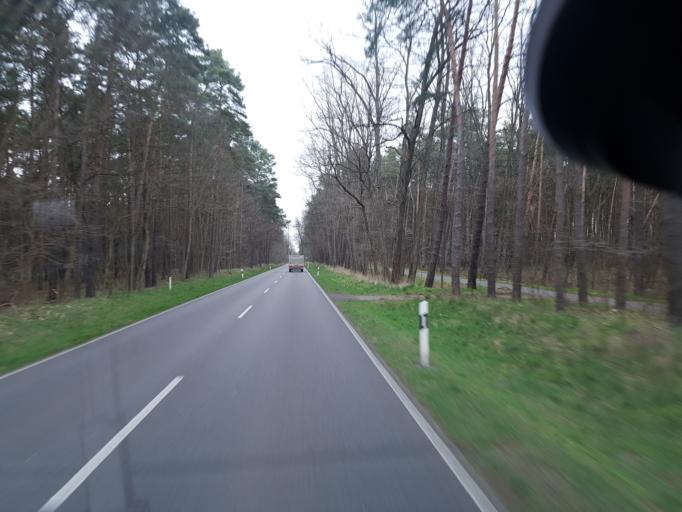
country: DE
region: Brandenburg
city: Tauche
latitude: 52.1281
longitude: 14.1976
